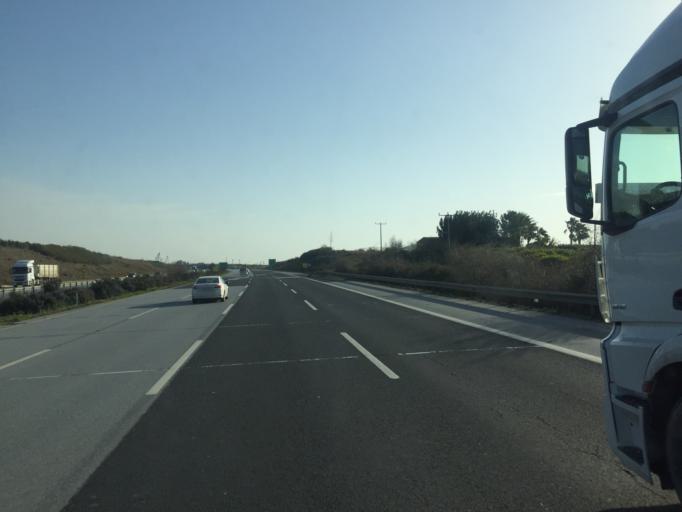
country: TR
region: Mersin
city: Yenice
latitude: 37.0231
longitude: 35.0949
